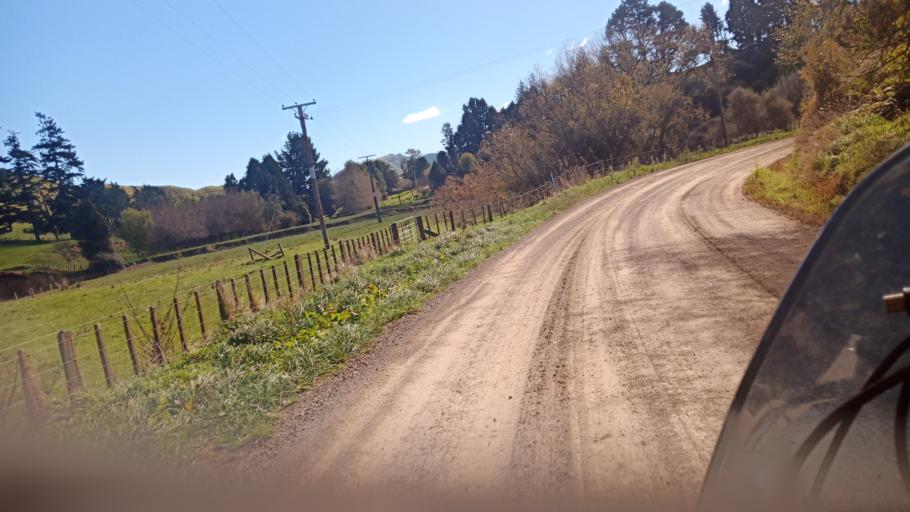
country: NZ
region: Bay of Plenty
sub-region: Opotiki District
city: Opotiki
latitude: -38.2966
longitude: 177.5525
